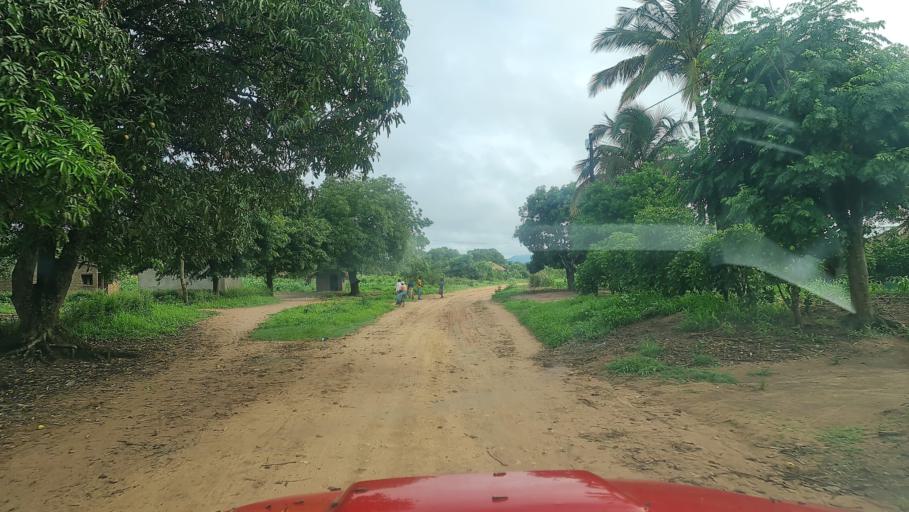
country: MW
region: Southern Region
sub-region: Nsanje District
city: Nsanje
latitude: -17.2957
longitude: 35.5942
